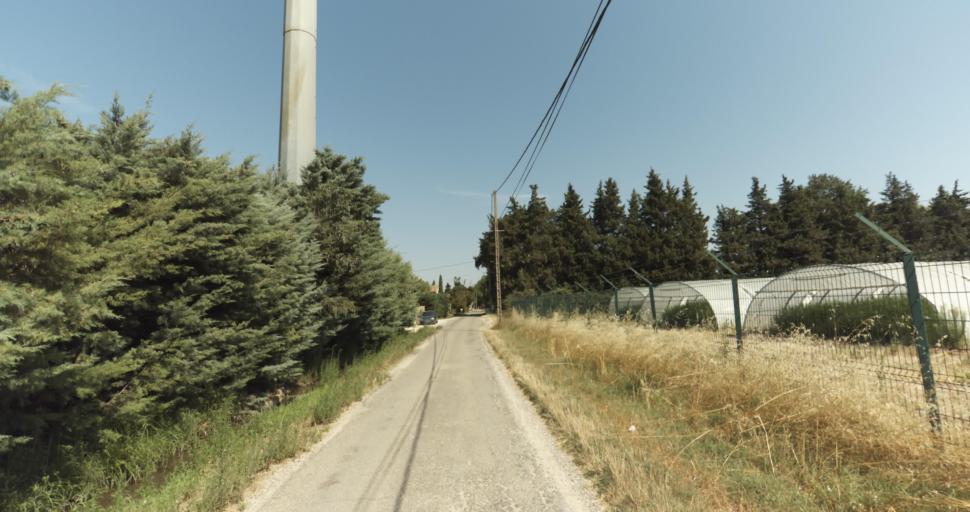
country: FR
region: Provence-Alpes-Cote d'Azur
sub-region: Departement du Vaucluse
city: Monteux
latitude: 44.0236
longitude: 5.0098
